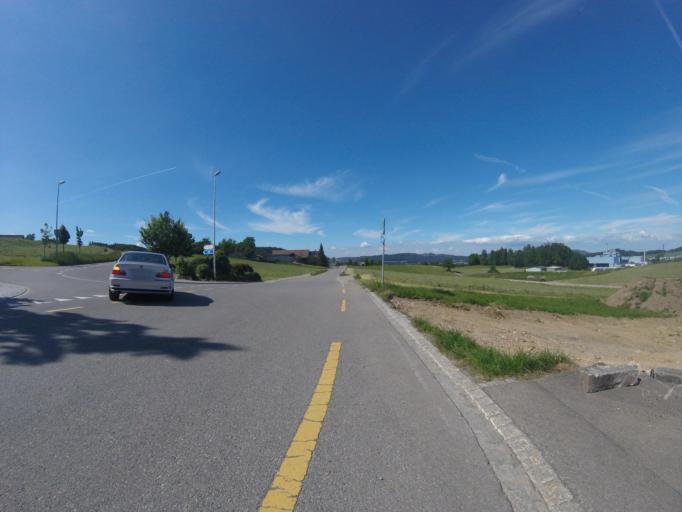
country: CH
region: Saint Gallen
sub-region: Wahlkreis Toggenburg
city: Kirchberg
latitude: 47.4201
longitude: 9.0623
